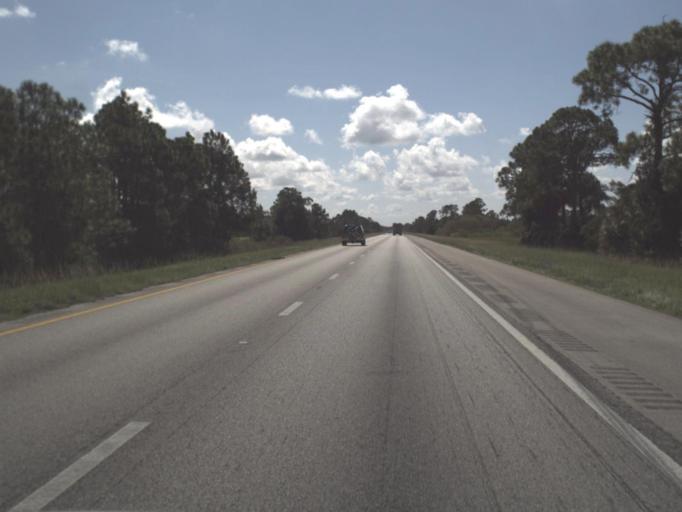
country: US
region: Florida
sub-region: Lee County
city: Burnt Store Marina
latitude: 26.8209
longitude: -81.9439
